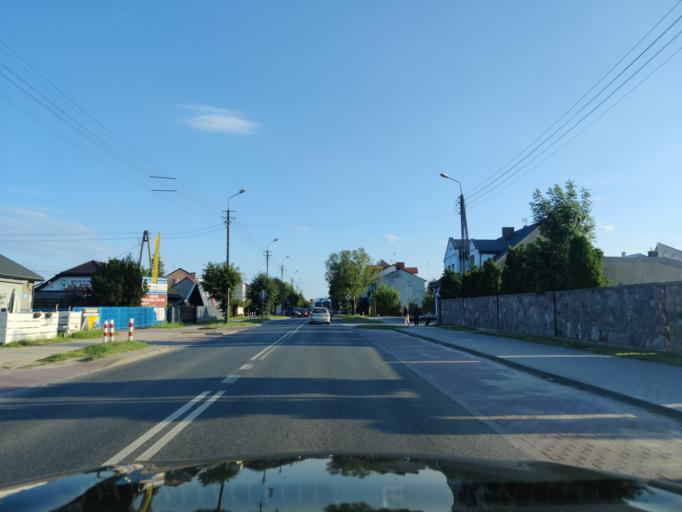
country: PL
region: Masovian Voivodeship
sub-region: Powiat pultuski
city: Pultusk
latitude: 52.7147
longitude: 21.0840
